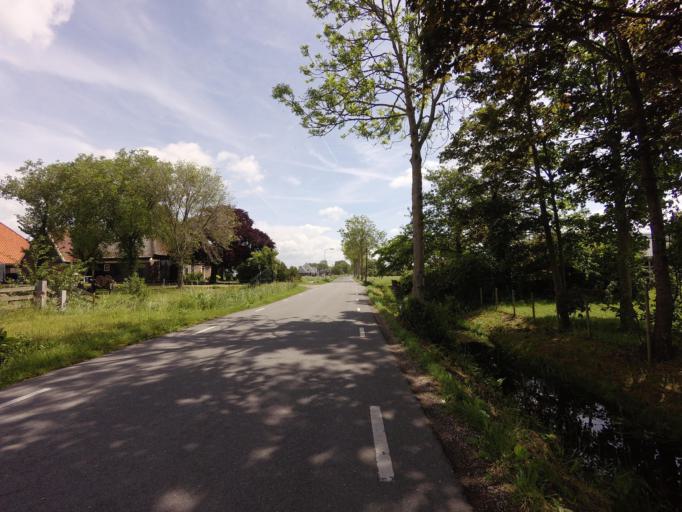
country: NL
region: North Holland
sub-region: Gemeente Hoorn
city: Hoorn
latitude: 52.6517
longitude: 4.9902
